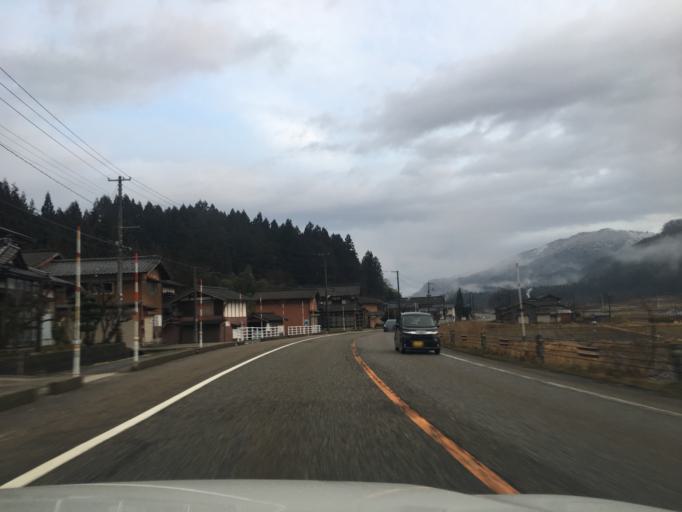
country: JP
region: Niigata
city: Murakami
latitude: 38.3449
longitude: 139.5497
